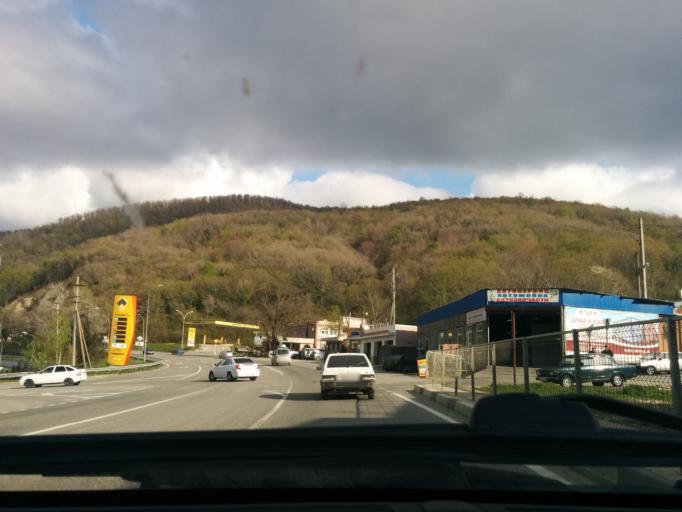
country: RU
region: Krasnodarskiy
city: Novomikhaylovskiy
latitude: 44.2564
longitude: 38.8662
